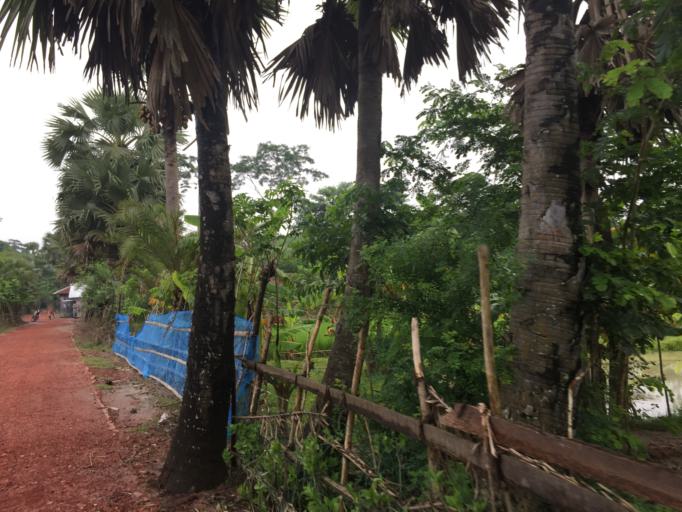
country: BD
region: Barisal
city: Mathba
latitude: 22.2038
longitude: 89.9376
